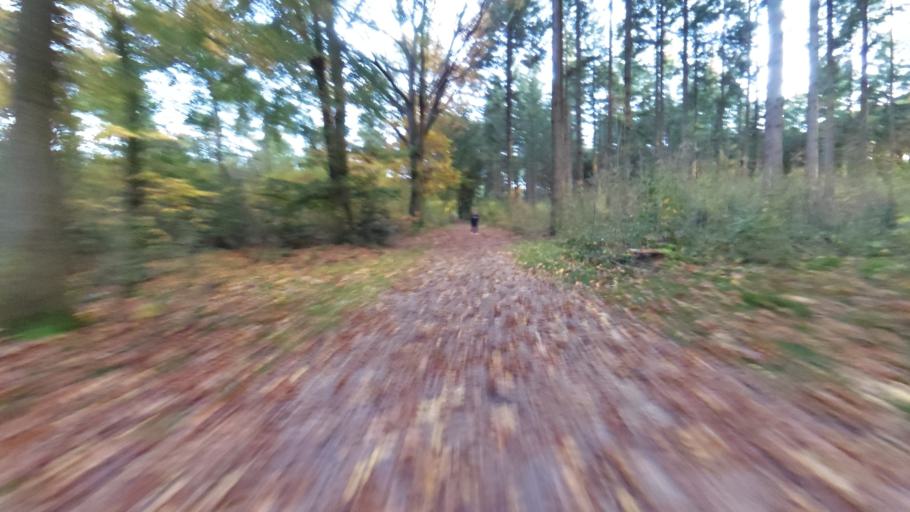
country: NL
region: Gelderland
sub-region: Gemeente Ede
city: Wekerom
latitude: 52.0914
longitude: 5.6712
